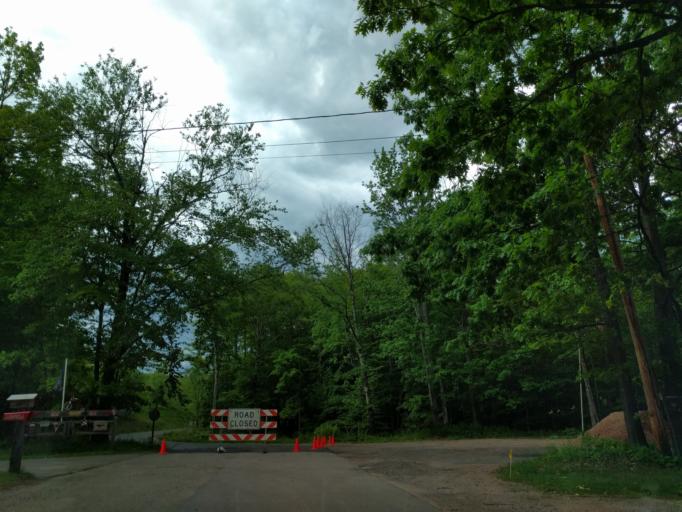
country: US
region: Michigan
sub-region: Marquette County
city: Trowbridge Park
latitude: 46.5572
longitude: -87.4474
